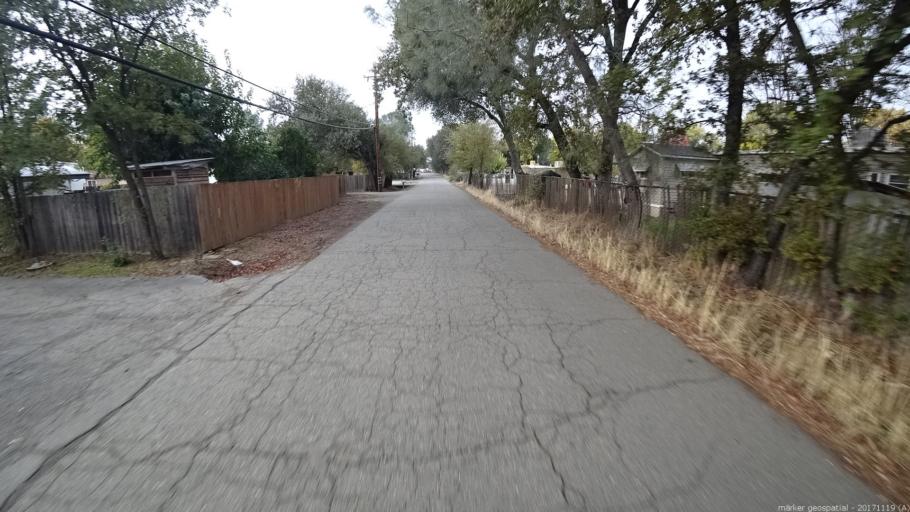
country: US
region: California
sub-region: Shasta County
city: Anderson
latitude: 40.4918
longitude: -122.3667
